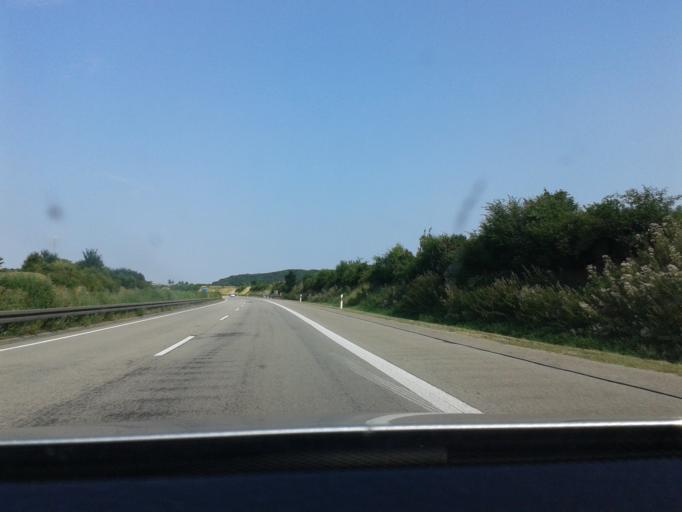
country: DE
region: Thuringia
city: Niedergebra
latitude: 51.4345
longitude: 10.6209
